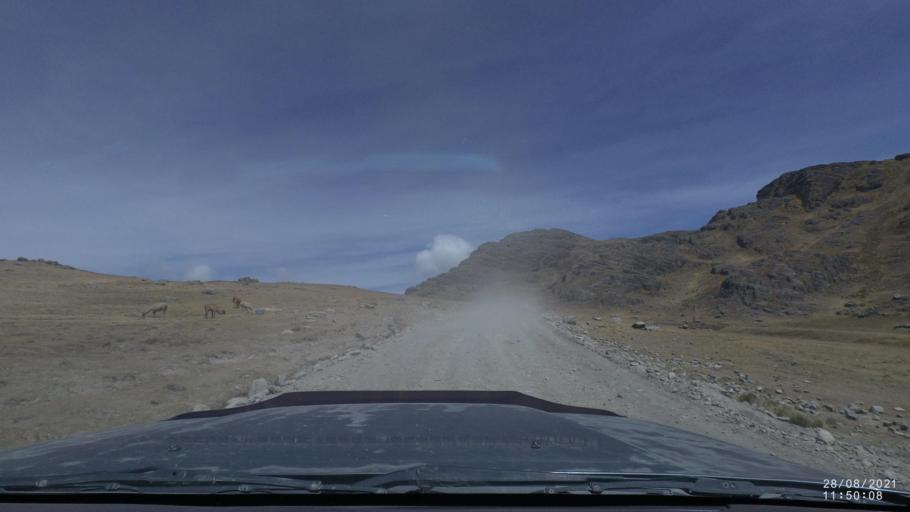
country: BO
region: Cochabamba
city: Sipe Sipe
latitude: -17.2323
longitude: -66.3908
